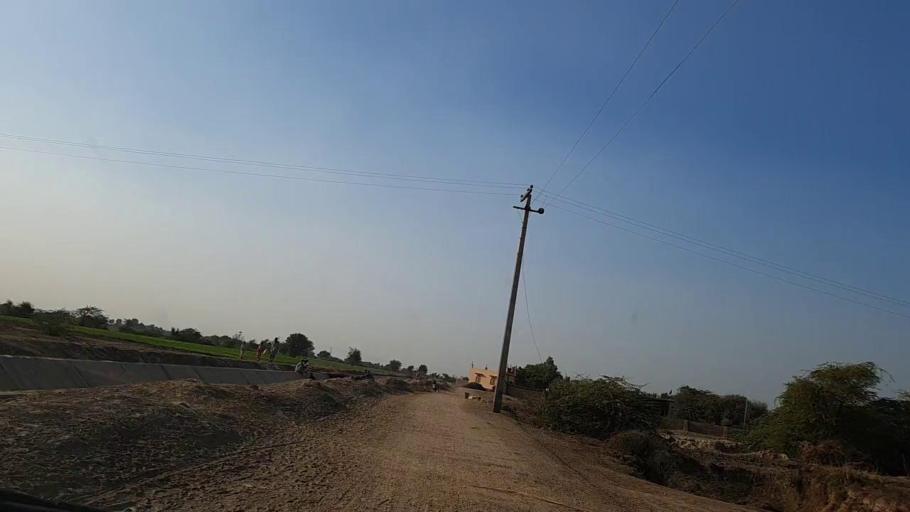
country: PK
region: Sindh
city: Sakrand
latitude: 26.0920
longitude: 68.2080
